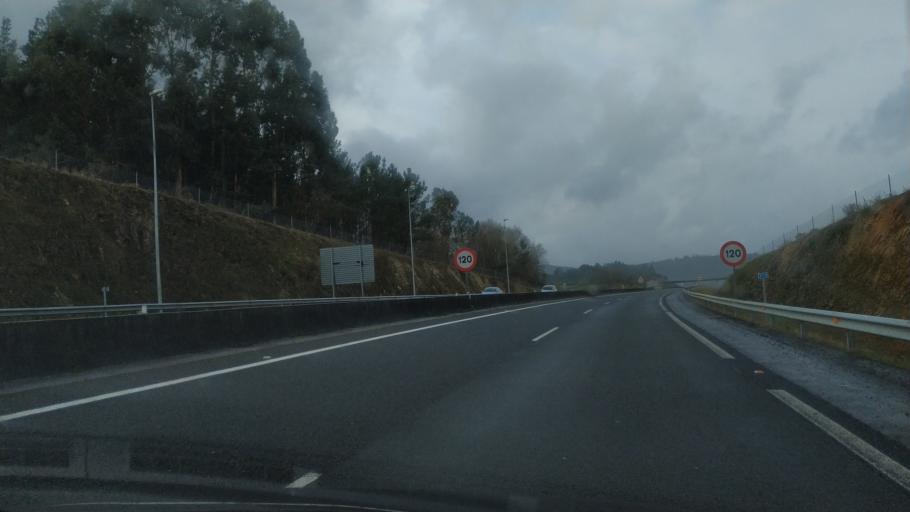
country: ES
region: Galicia
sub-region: Provincia de Pontevedra
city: Silleda
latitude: 42.7182
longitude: -8.3056
